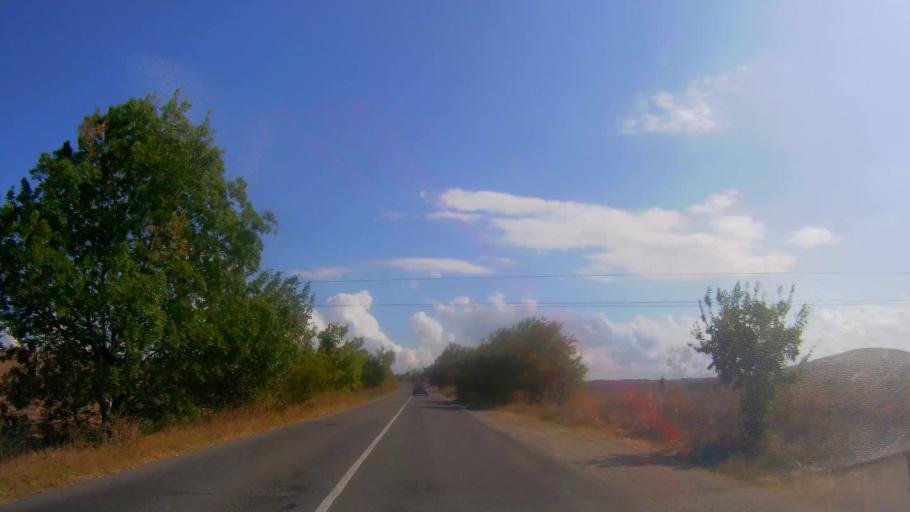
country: BG
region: Burgas
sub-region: Obshtina Burgas
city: Burgas
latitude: 42.4791
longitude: 27.3887
